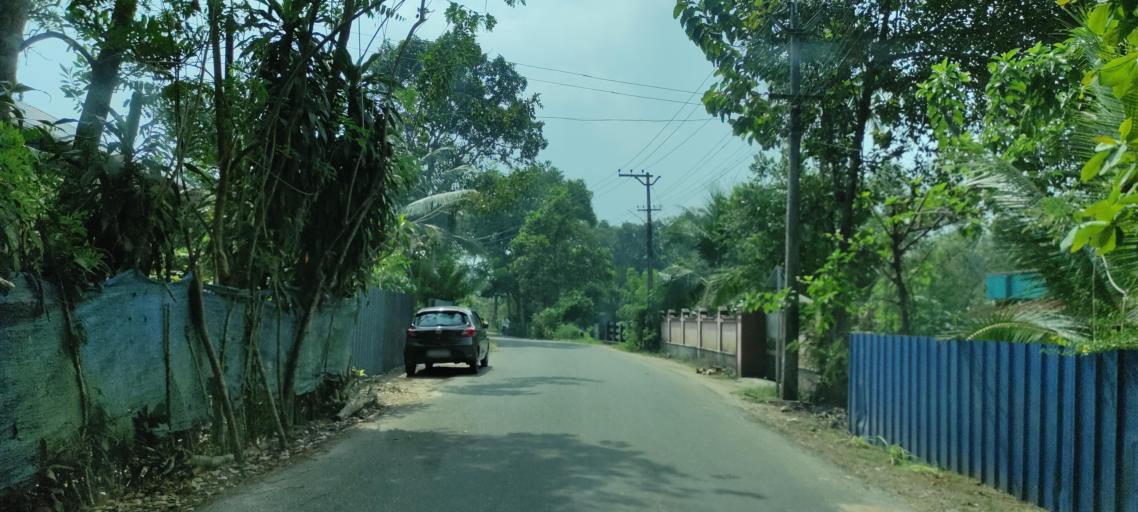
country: IN
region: Kerala
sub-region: Alappuzha
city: Shertallai
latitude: 9.6127
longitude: 76.3480
